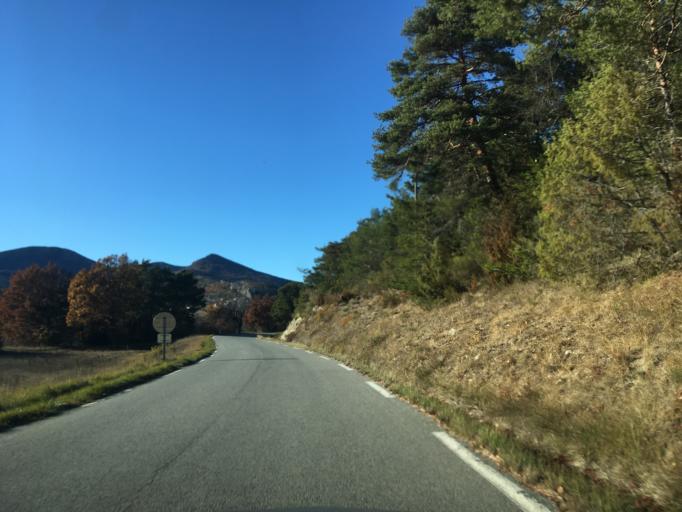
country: FR
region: Provence-Alpes-Cote d'Azur
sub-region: Departement des Alpes-de-Haute-Provence
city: Castellane
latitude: 43.7552
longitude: 6.4635
